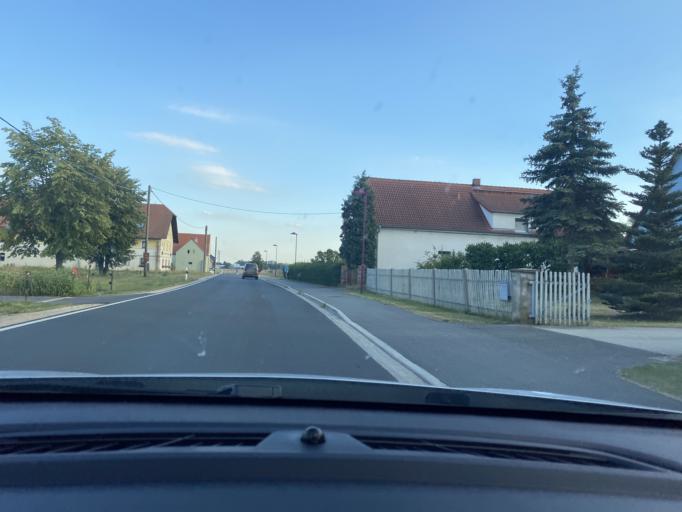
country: DE
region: Saxony
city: Kodersdorf
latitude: 51.2569
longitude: 14.8875
